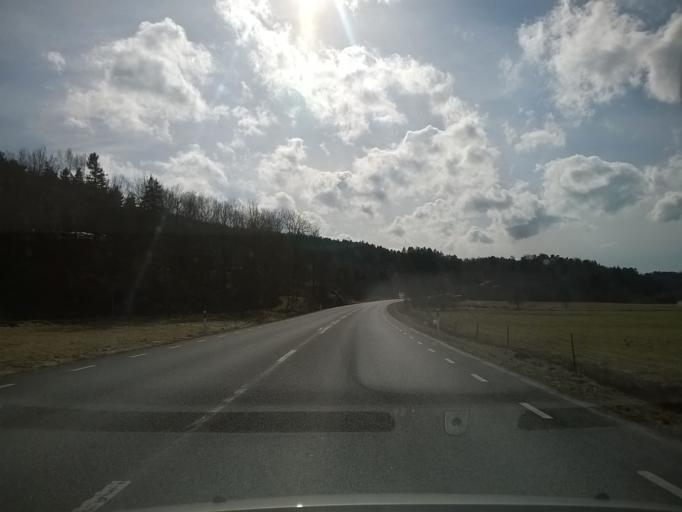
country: SE
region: Vaestra Goetaland
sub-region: Orust
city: Henan
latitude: 58.2720
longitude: 11.6935
